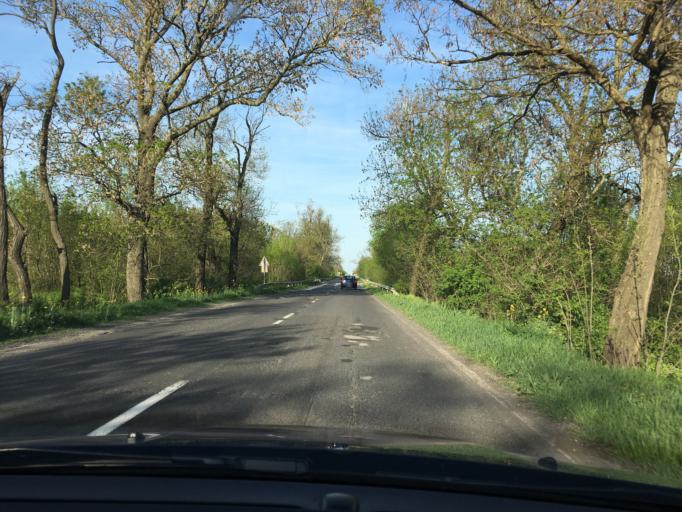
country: HU
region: Hajdu-Bihar
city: Csokmo
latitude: 47.0085
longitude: 21.2371
